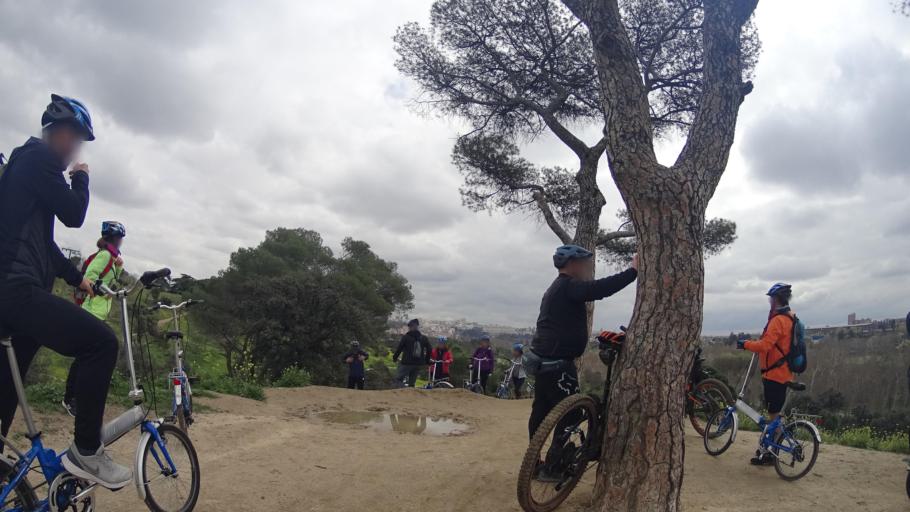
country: ES
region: Madrid
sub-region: Provincia de Madrid
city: Moncloa-Aravaca
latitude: 40.4198
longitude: -3.7435
